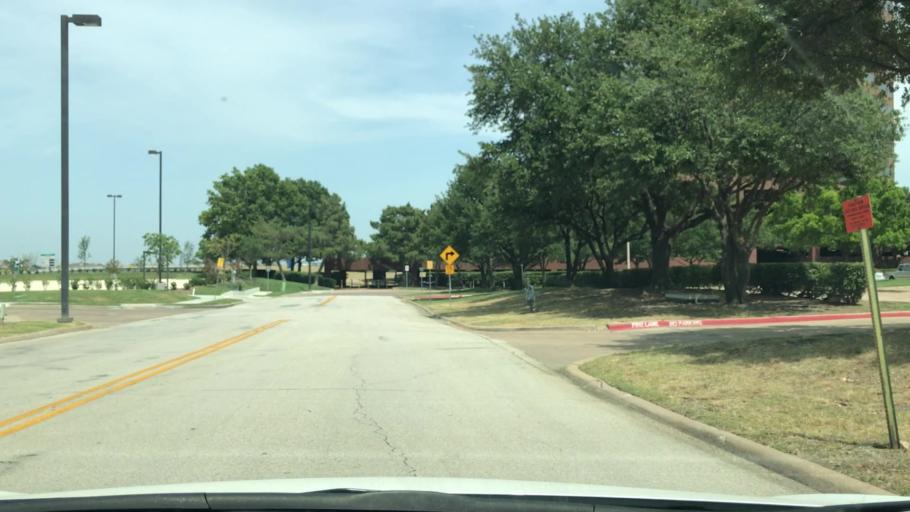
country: US
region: Texas
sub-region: Dallas County
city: Irving
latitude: 32.8896
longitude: -96.9666
